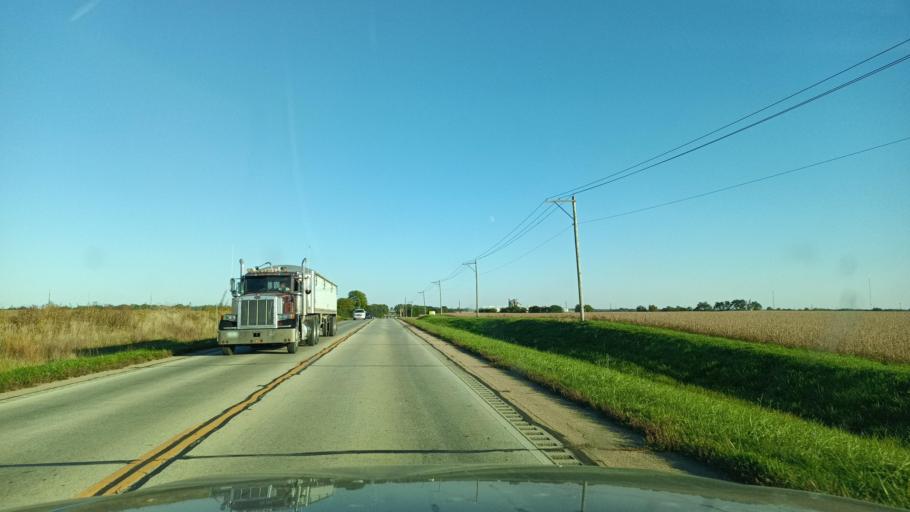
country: US
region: Illinois
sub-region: Champaign County
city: Lake of the Woods
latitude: 40.1757
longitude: -88.3467
